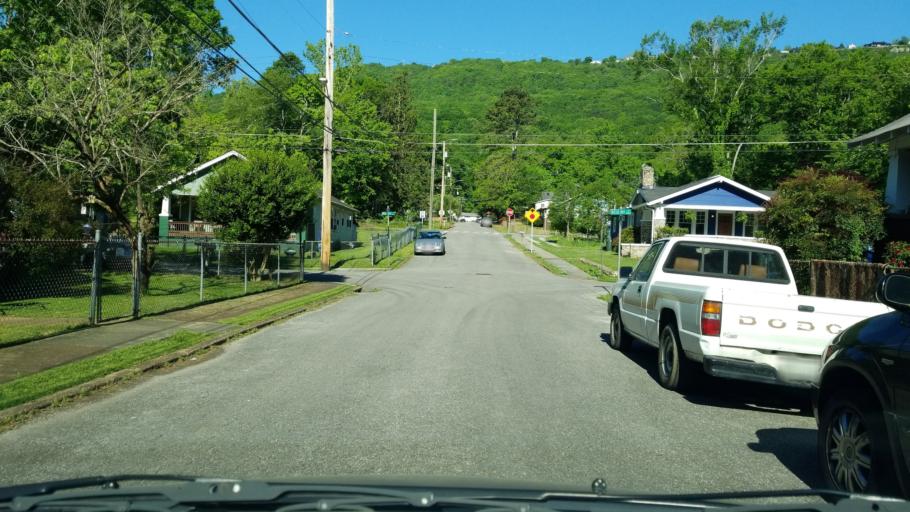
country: US
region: Tennessee
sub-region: Hamilton County
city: Lookout Mountain
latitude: 34.9924
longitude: -85.3292
